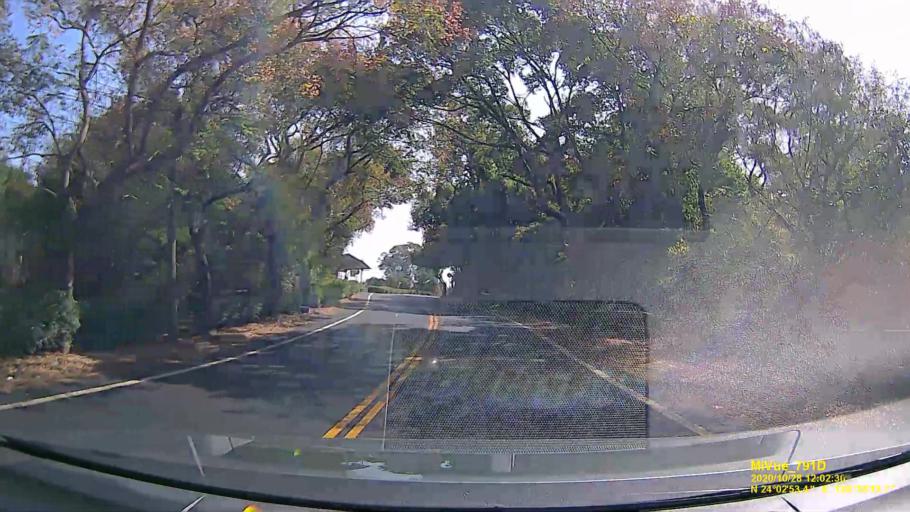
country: TW
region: Taiwan
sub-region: Changhua
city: Chang-hua
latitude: 24.0482
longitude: 120.5871
